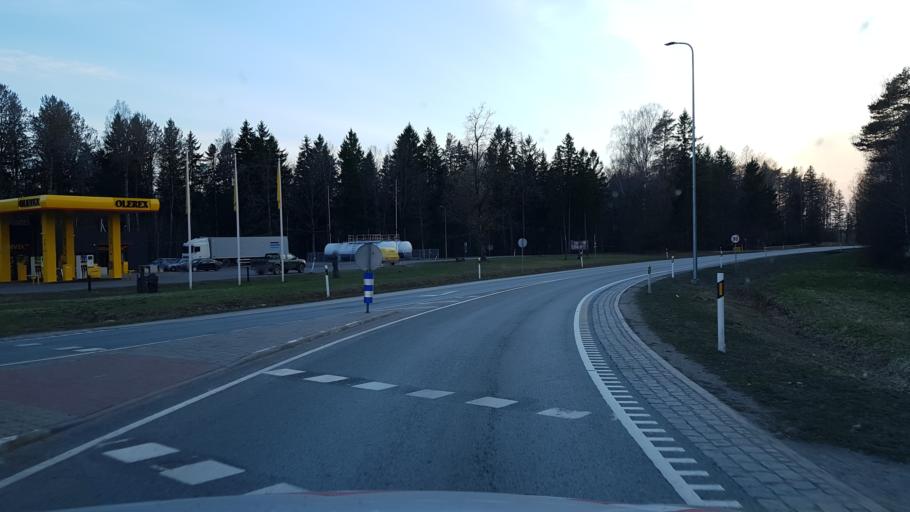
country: EE
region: Laeaene-Virumaa
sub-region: Rakvere linn
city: Rakvere
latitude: 59.3207
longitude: 26.3704
